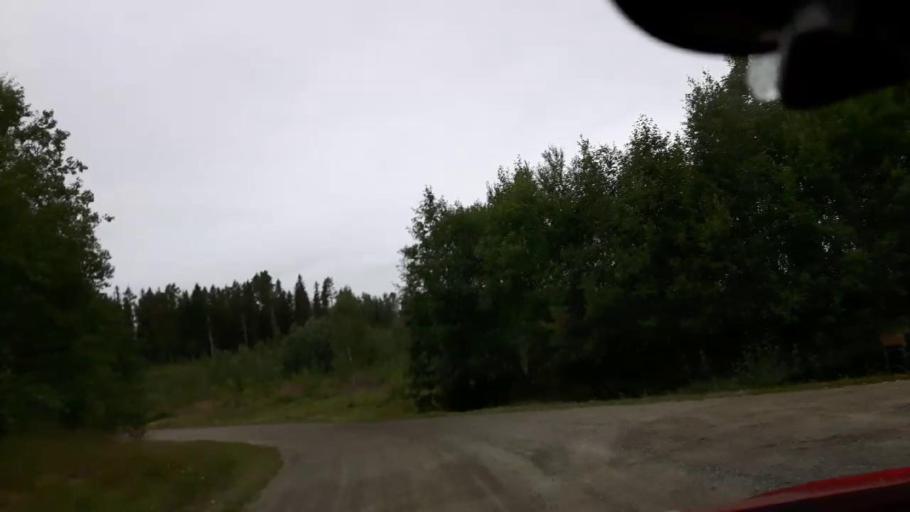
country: SE
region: Vaesternorrland
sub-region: Ange Kommun
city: Ange
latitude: 62.8568
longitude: 15.9092
